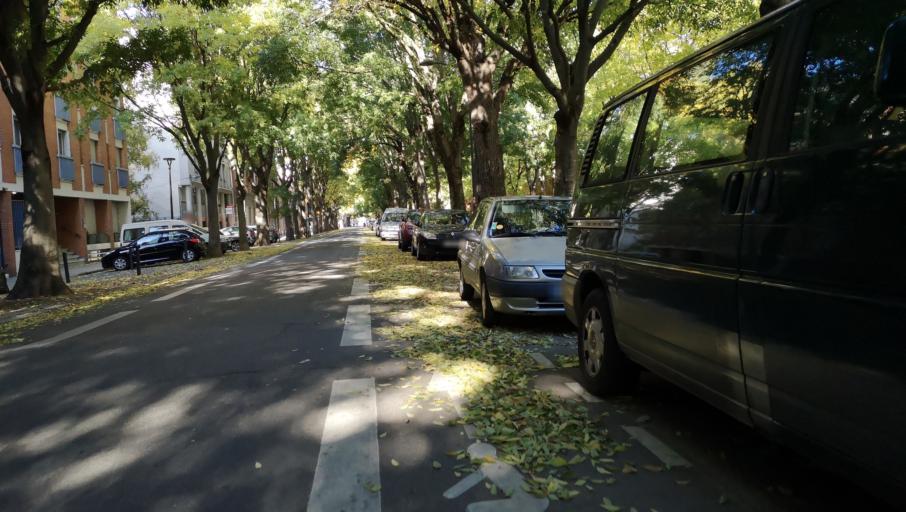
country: FR
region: Midi-Pyrenees
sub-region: Departement de la Haute-Garonne
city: Toulouse
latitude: 43.6061
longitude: 1.4347
